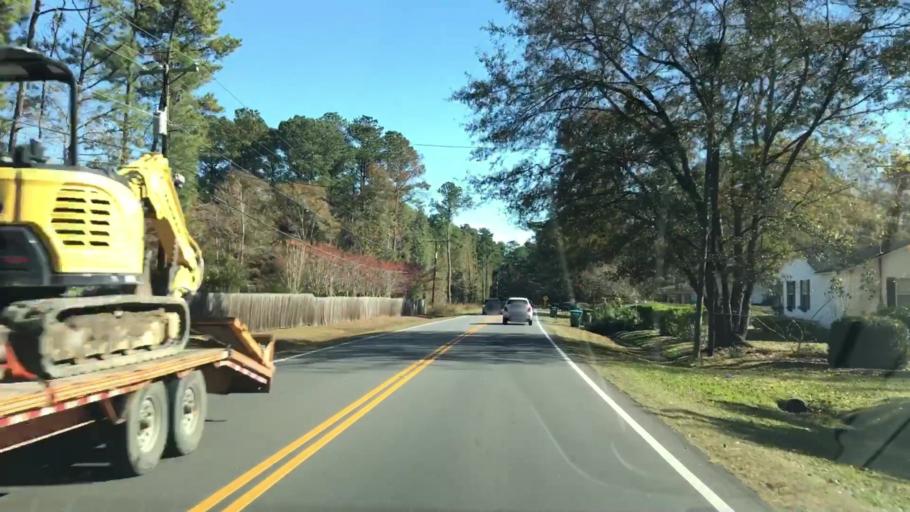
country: US
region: South Carolina
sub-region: Dorchester County
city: Summerville
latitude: 33.0231
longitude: -80.2001
